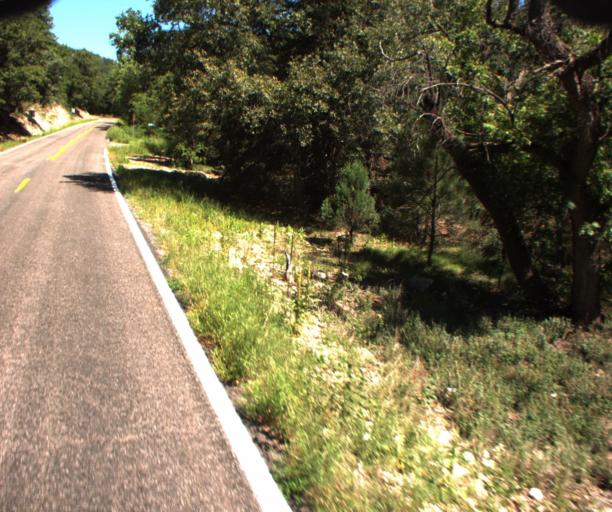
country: US
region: Arizona
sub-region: Greenlee County
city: Morenci
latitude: 33.1841
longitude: -109.3816
